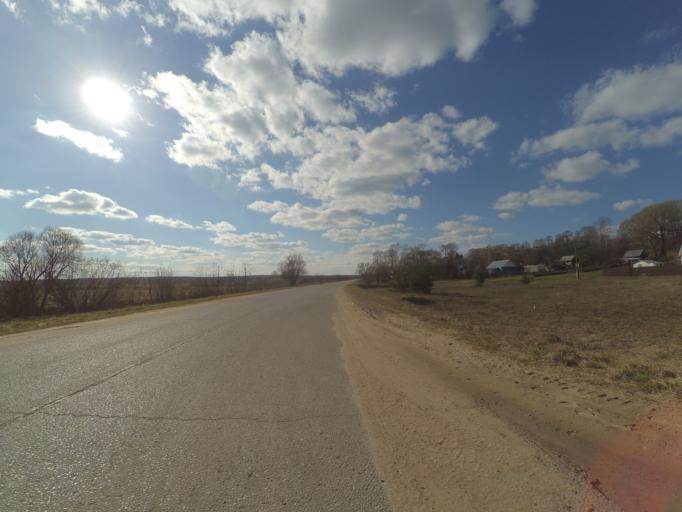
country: RU
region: Moskovskaya
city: Bol'shoye Gryzlovo
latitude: 54.8683
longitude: 37.8448
